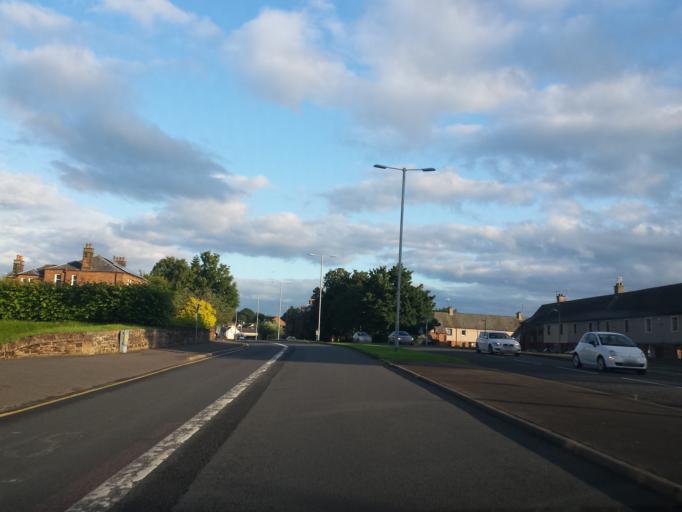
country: GB
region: Scotland
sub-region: Dumfries and Galloway
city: Dumfries
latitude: 55.0724
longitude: -3.6214
